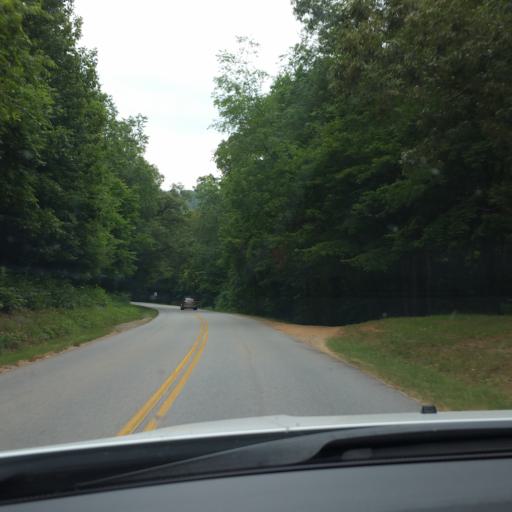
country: US
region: North Carolina
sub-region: Buncombe County
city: Biltmore Forest
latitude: 35.5639
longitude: -82.4876
